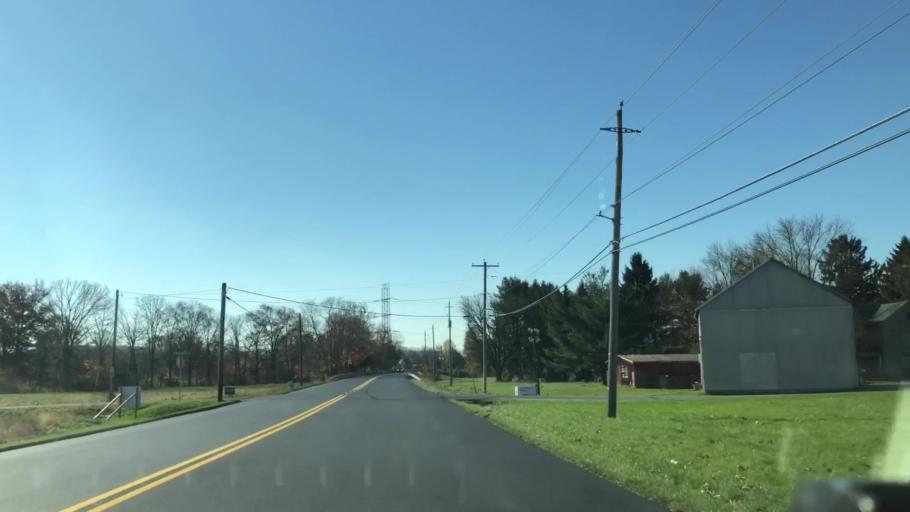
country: US
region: Pennsylvania
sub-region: Berks County
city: Bally
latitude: 40.4442
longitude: -75.5542
